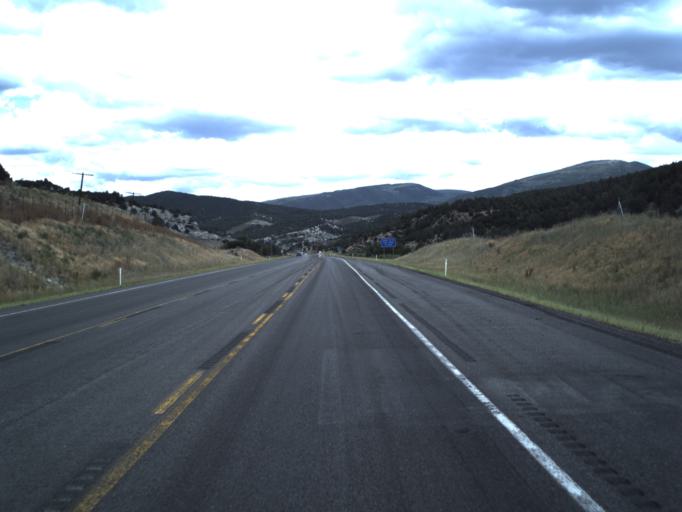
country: US
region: Utah
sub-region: Sanpete County
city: Fairview
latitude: 39.9526
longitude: -111.2255
